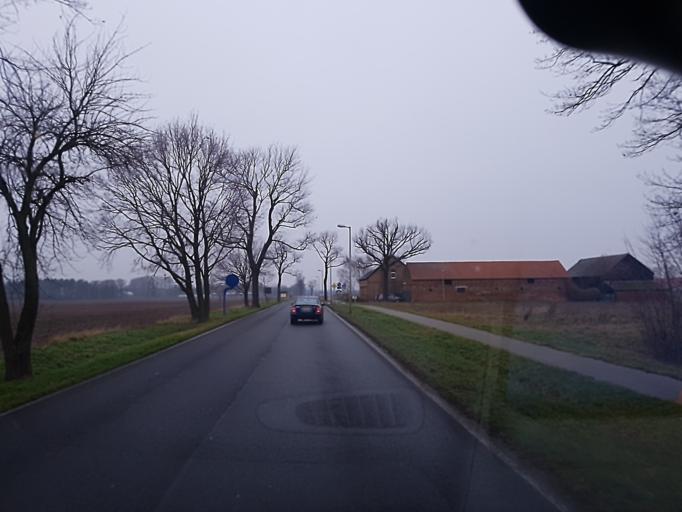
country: DE
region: Brandenburg
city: Lubbenau
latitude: 51.8699
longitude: 13.9168
